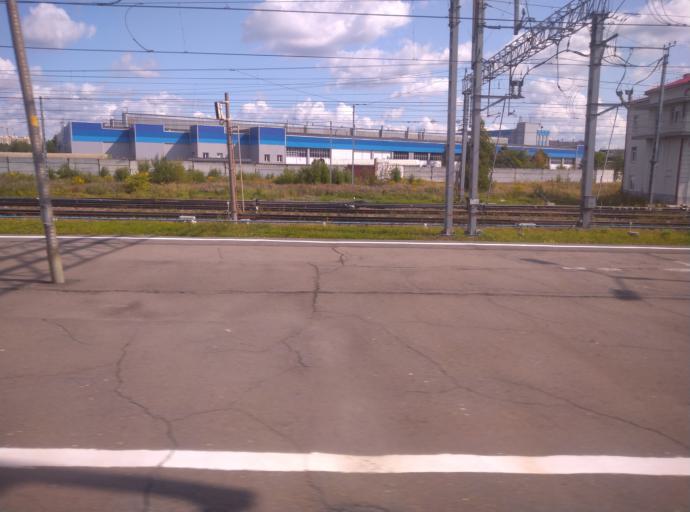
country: RU
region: St.-Petersburg
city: Obukhovo
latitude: 59.8496
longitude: 30.4530
